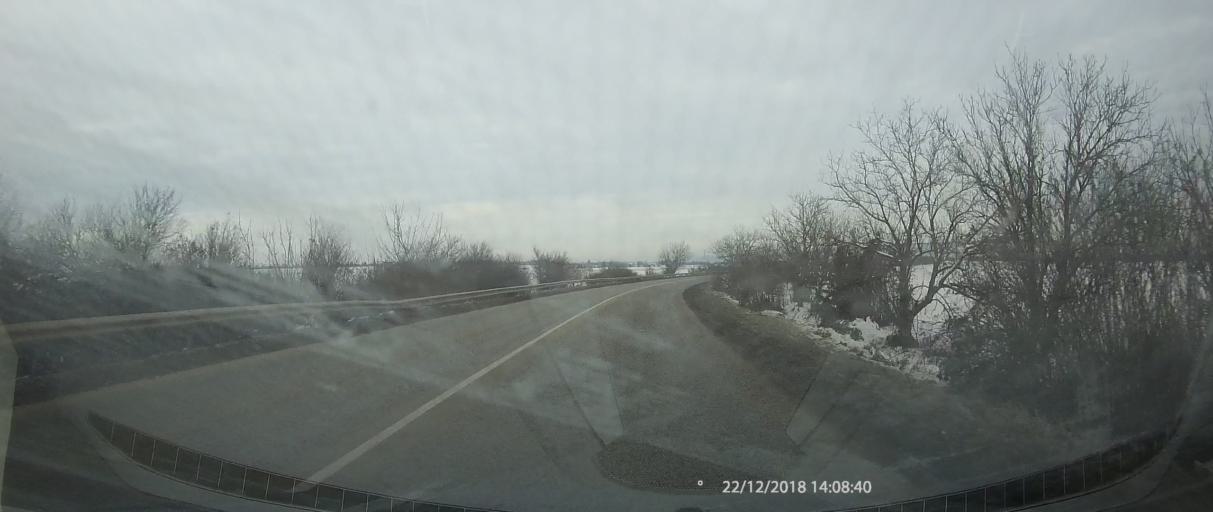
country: BG
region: Pleven
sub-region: Obshtina Dolna Mitropoliya
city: Dolna Mitropoliya
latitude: 43.4296
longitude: 24.5027
